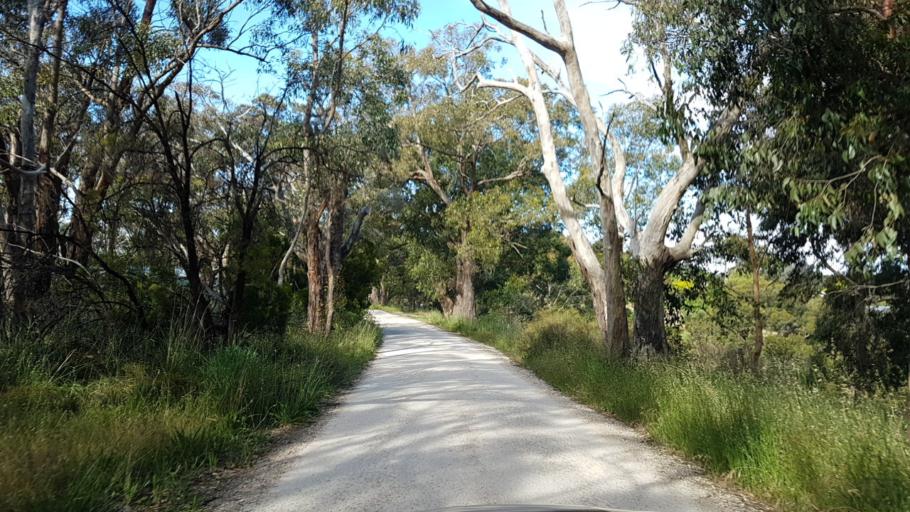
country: AU
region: South Australia
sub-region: Adelaide Hills
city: Adelaide Hills
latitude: -34.9061
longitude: 138.7394
